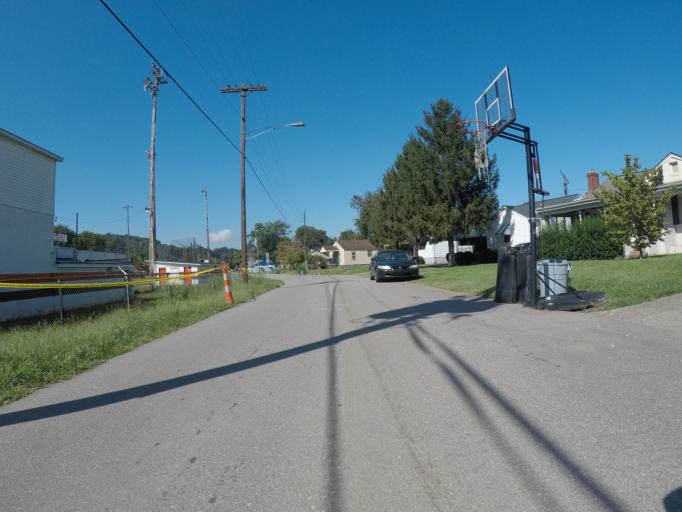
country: US
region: Ohio
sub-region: Lawrence County
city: Burlington
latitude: 38.3986
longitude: -82.5115
